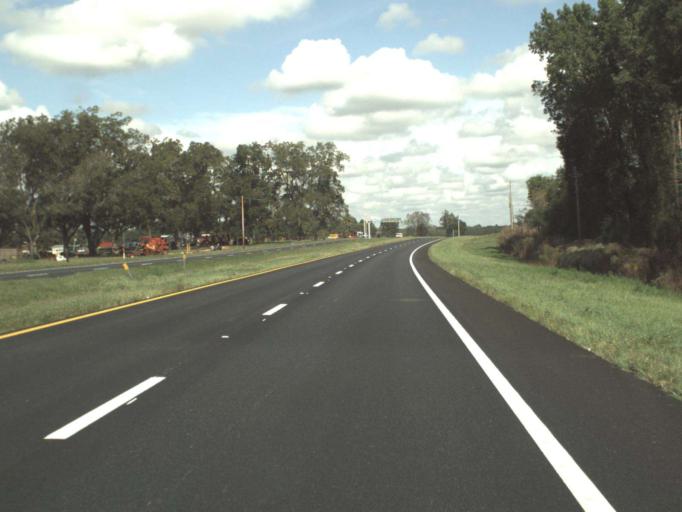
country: US
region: Florida
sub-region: Jackson County
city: Graceville
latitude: 30.9700
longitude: -85.4085
